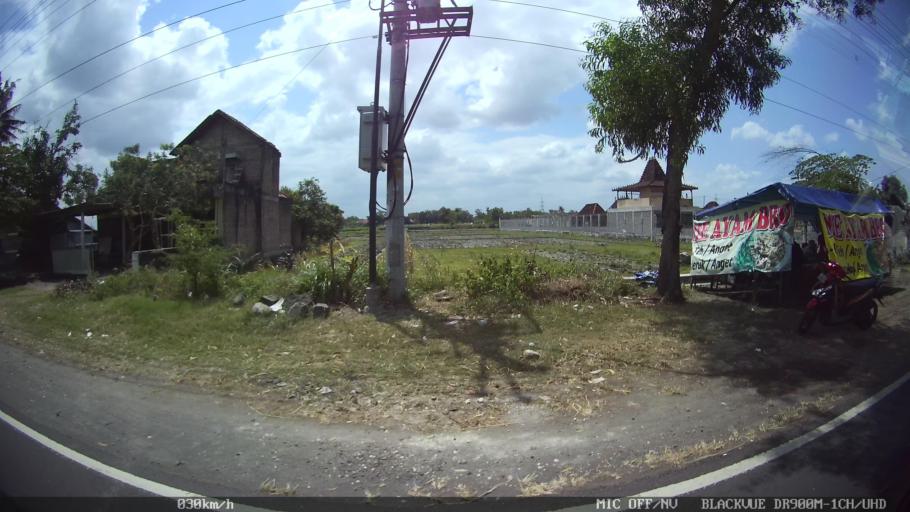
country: ID
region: Daerah Istimewa Yogyakarta
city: Bantul
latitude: -7.8811
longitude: 110.3400
